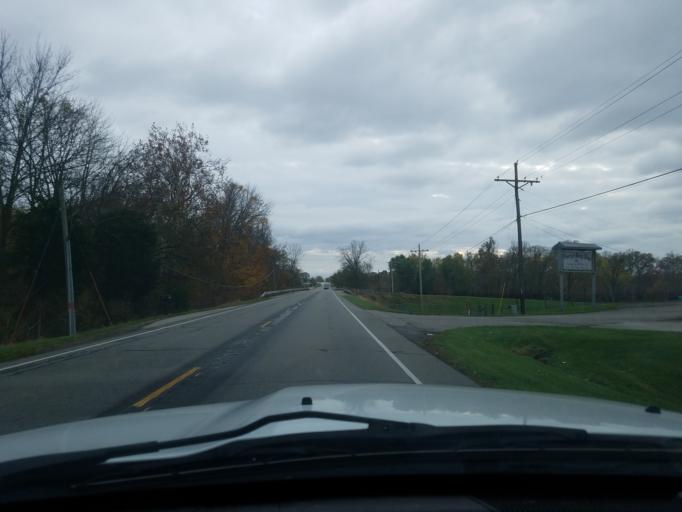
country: US
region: Indiana
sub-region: Bartholomew County
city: Hope
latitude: 39.2358
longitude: -85.7718
